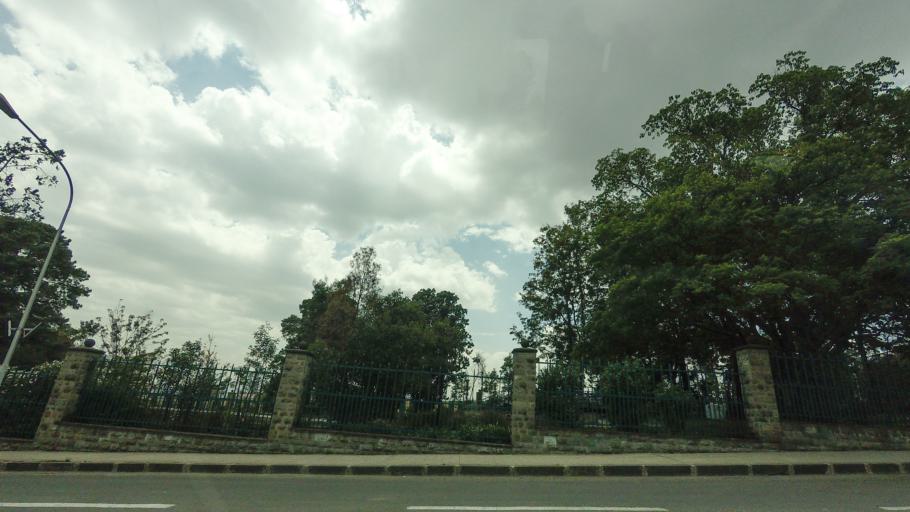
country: ET
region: Adis Abeba
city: Addis Ababa
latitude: 9.0208
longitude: 38.7640
